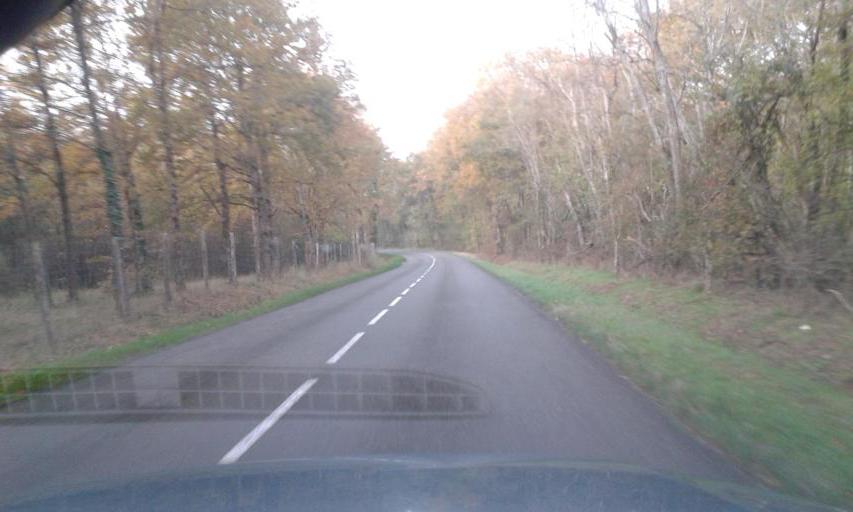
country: FR
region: Centre
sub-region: Departement du Loiret
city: Dry
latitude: 47.7543
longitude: 1.7507
